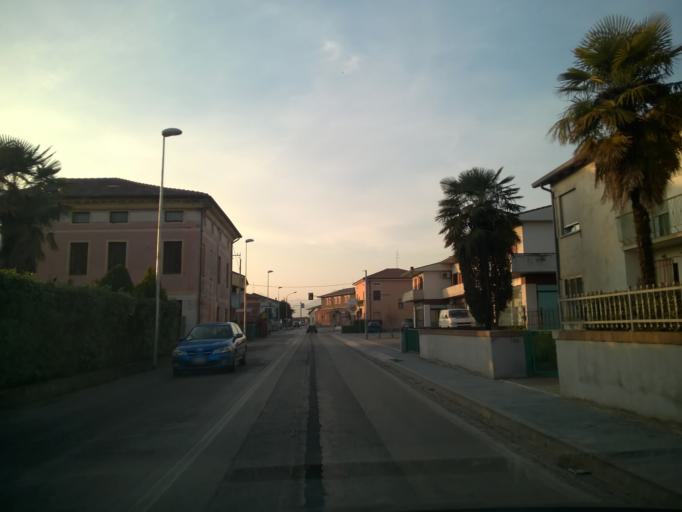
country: IT
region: Veneto
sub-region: Provincia di Vicenza
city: Caldogno-Rettorgole-Cresole
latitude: 45.6228
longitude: 11.5072
